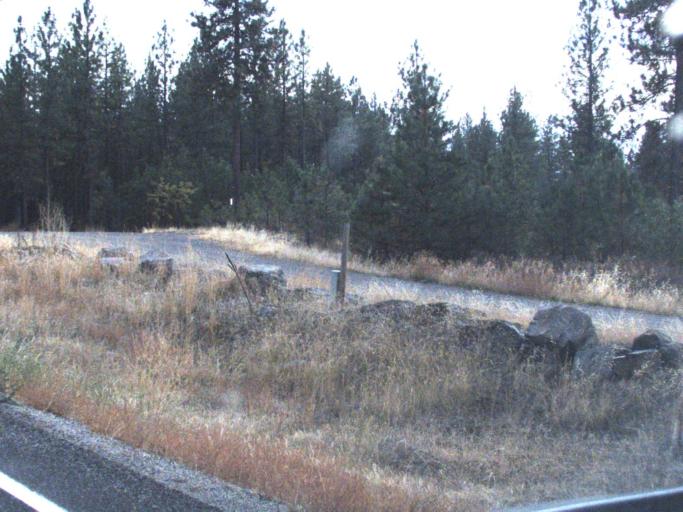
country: US
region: Washington
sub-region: Lincoln County
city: Davenport
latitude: 48.0822
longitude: -118.2014
